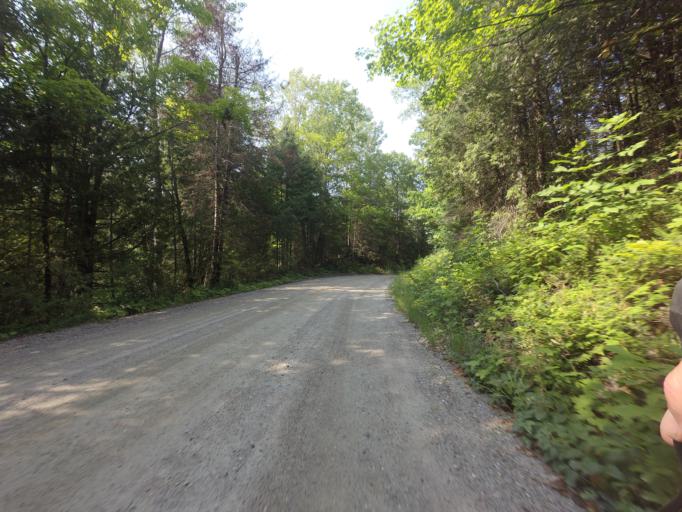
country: CA
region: Ontario
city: Skatepark
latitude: 44.7589
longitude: -76.8240
